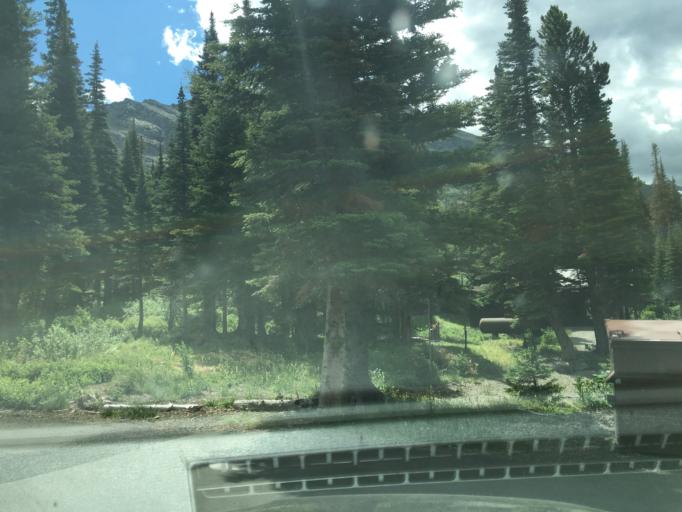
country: US
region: Montana
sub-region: Glacier County
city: South Browning
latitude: 48.4838
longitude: -113.3694
